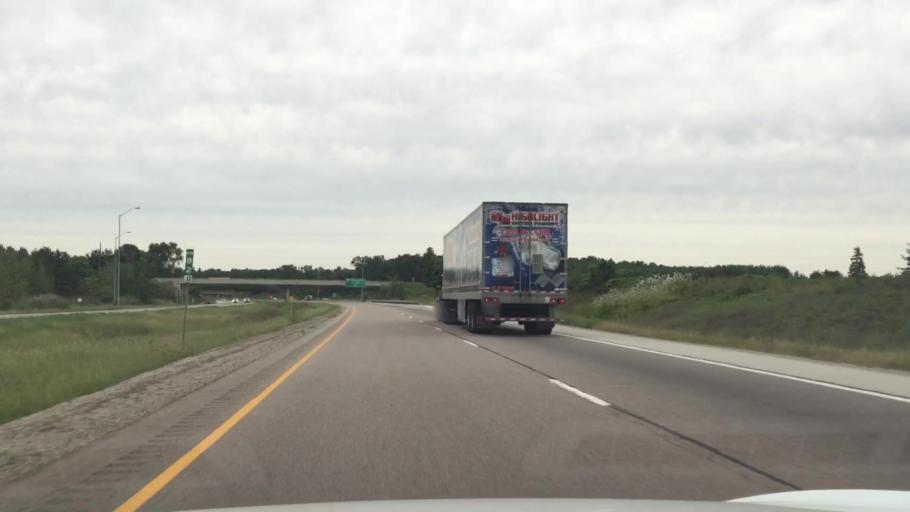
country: CA
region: Ontario
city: Delaware
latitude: 42.9200
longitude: -81.4604
